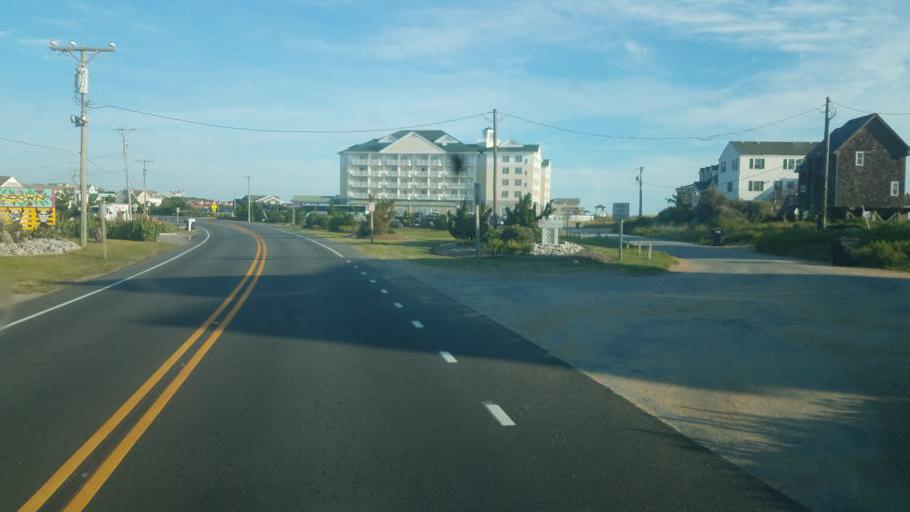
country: US
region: North Carolina
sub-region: Dare County
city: Kitty Hawk
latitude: 36.0990
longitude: -75.7105
